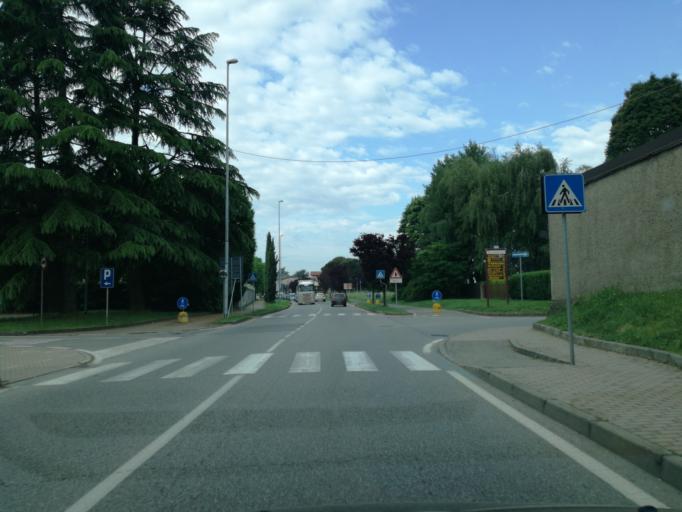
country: IT
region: Lombardy
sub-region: Provincia di Monza e Brianza
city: Albiate
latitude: 45.6566
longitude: 9.2506
